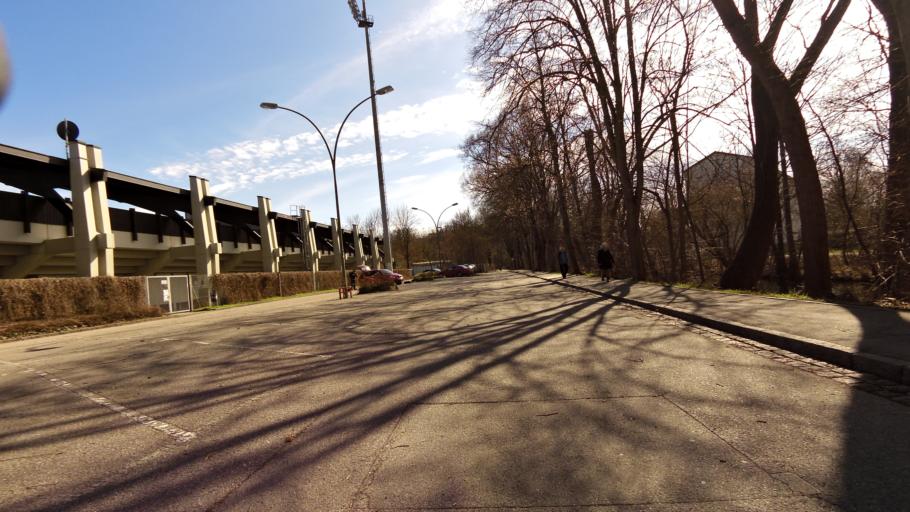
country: DE
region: Bavaria
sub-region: Lower Bavaria
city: Landshut
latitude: 48.5326
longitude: 12.1373
